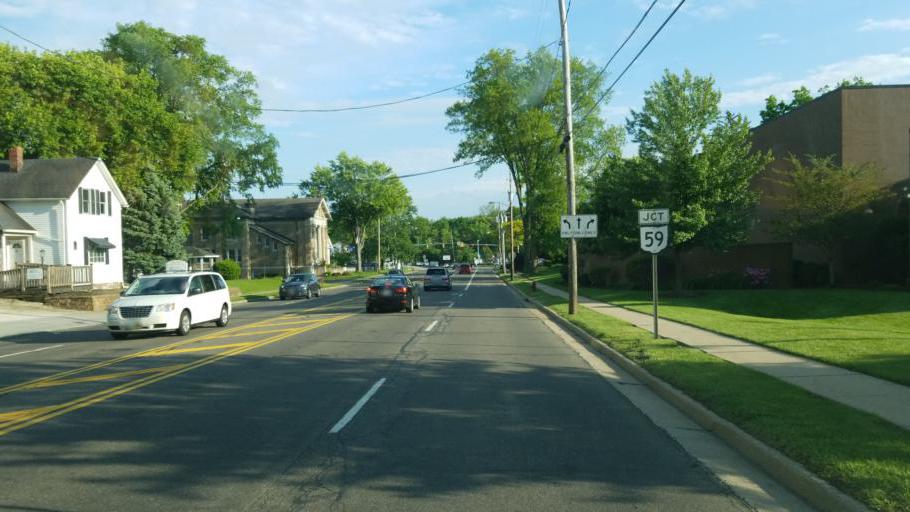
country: US
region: Ohio
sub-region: Summit County
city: Stow
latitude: 41.1612
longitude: -81.4405
